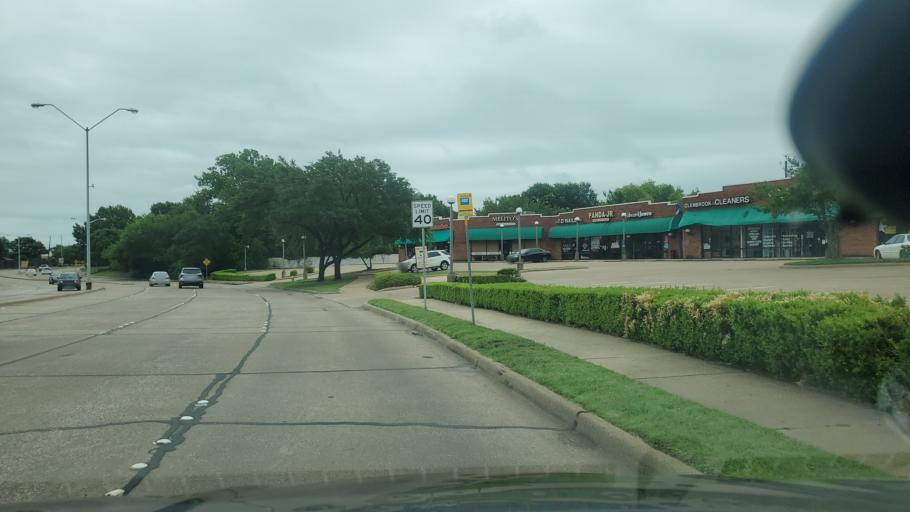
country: US
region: Texas
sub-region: Dallas County
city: Garland
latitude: 32.9402
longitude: -96.6398
